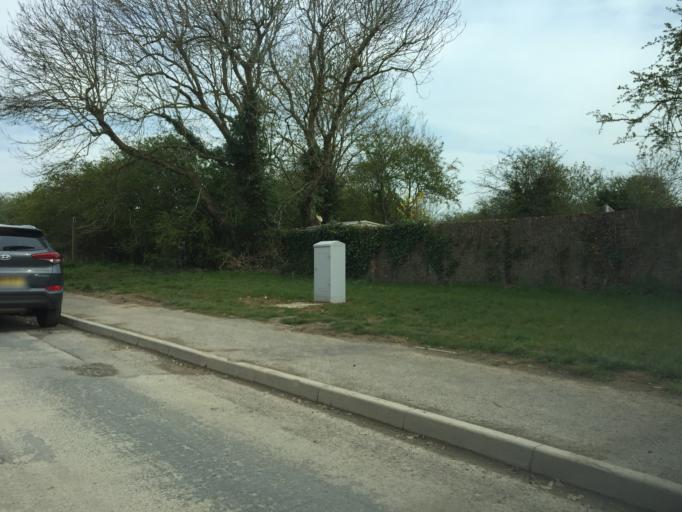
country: GB
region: England
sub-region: South Gloucestershire
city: Almondsbury
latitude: 51.5161
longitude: -2.5951
